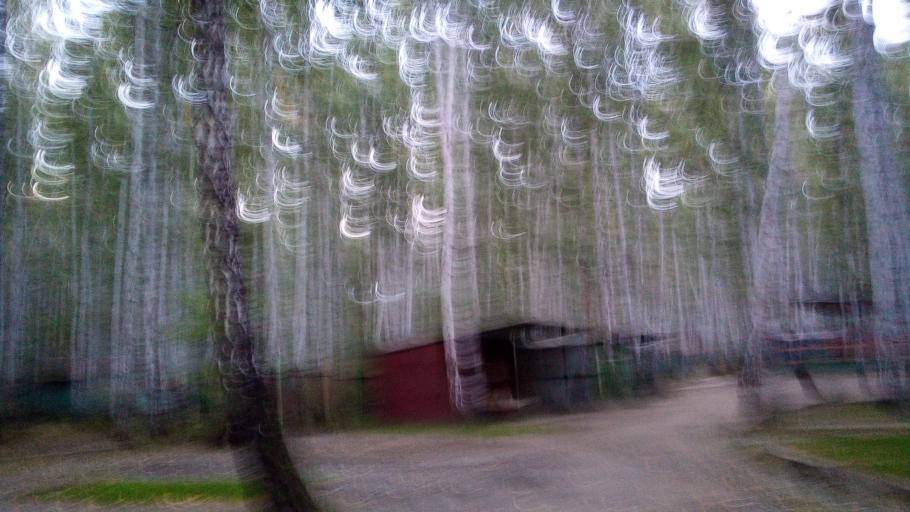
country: RU
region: Chelyabinsk
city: Tayginka
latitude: 55.4766
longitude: 60.4989
